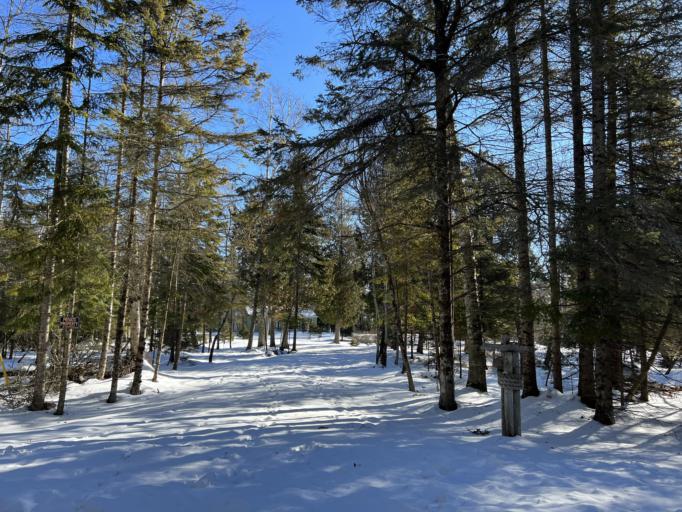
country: US
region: Michigan
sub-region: Delta County
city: Escanaba
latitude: 45.3528
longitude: -86.8699
